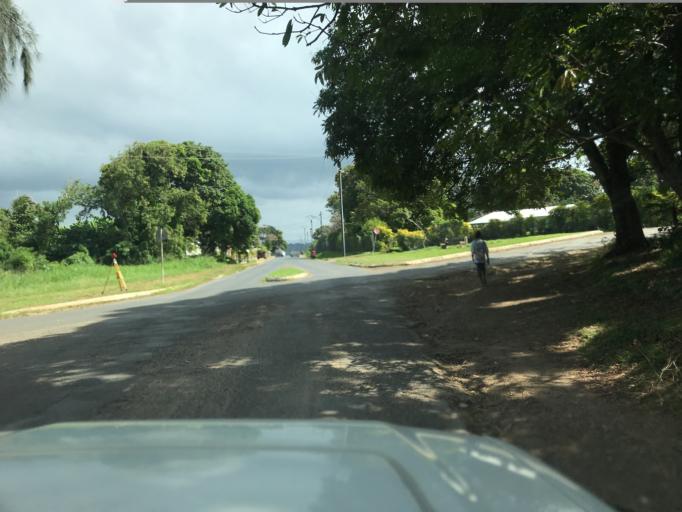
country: VU
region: Sanma
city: Luganville
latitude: -15.5104
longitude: 167.1848
